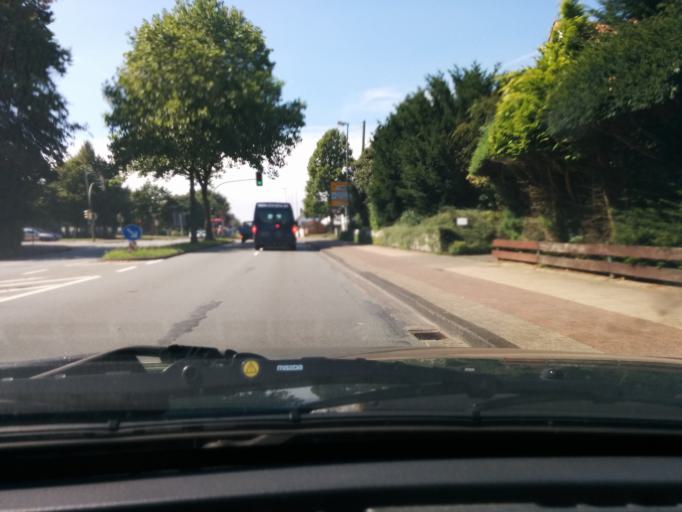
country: DE
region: North Rhine-Westphalia
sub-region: Regierungsbezirk Detmold
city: Bielefeld
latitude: 52.0580
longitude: 8.5208
